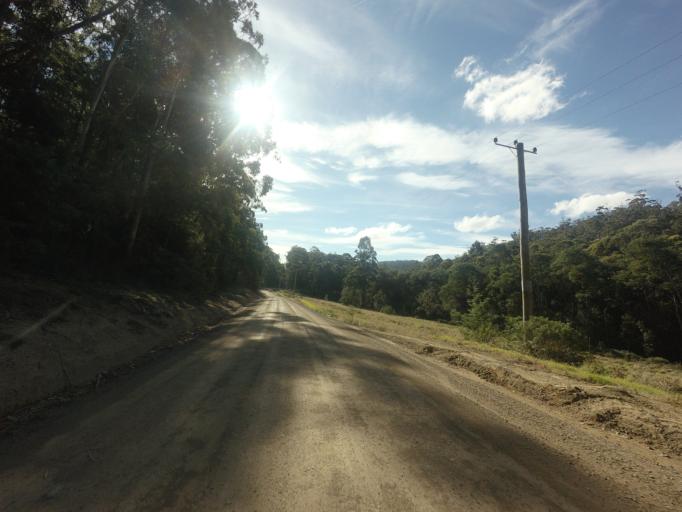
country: AU
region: Tasmania
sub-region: Clarence
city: Sandford
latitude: -43.1291
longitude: 147.7633
